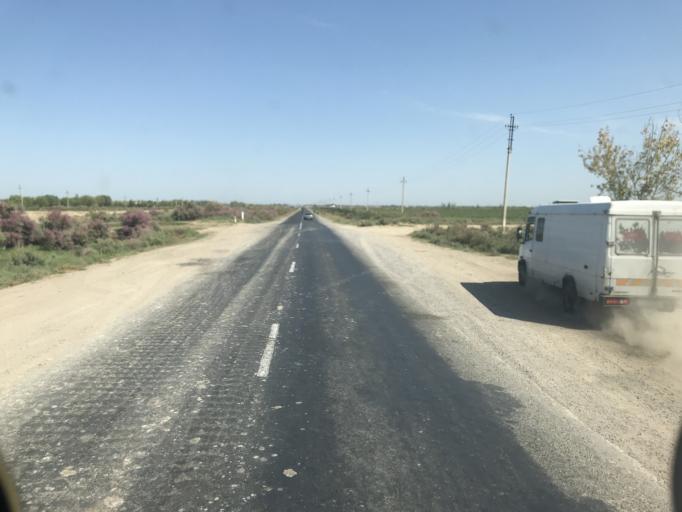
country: KZ
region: Ongtustik Qazaqstan
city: Myrzakent
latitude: 40.7331
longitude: 68.5366
